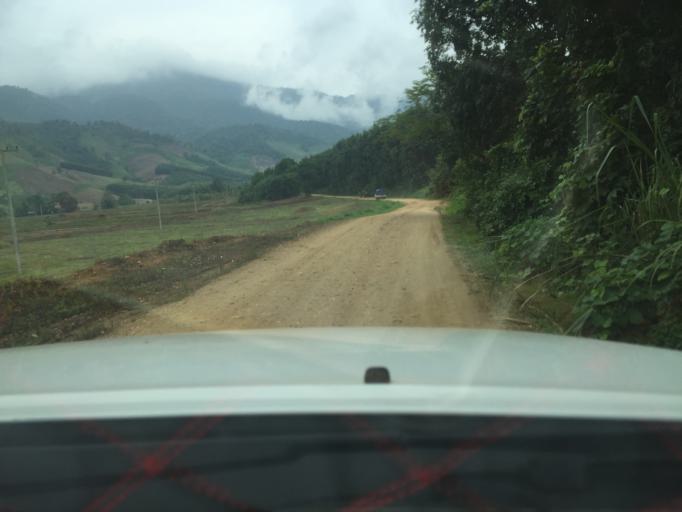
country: TH
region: Phayao
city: Phu Sang
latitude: 19.7417
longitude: 100.4462
